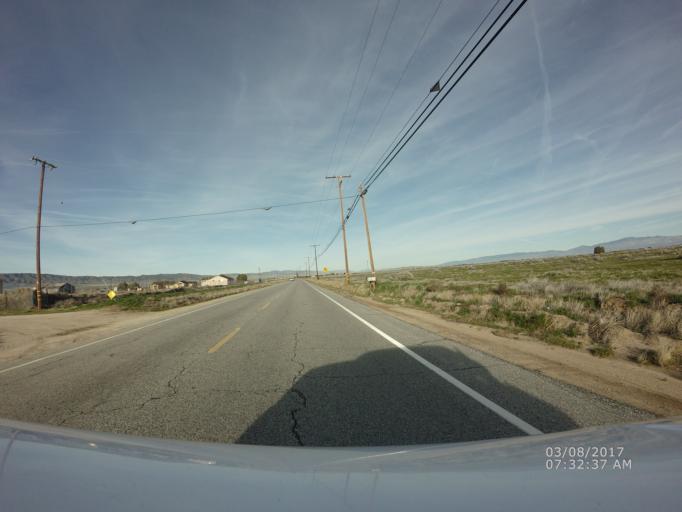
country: US
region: California
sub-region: Los Angeles County
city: Quartz Hill
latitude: 34.7042
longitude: -118.2610
